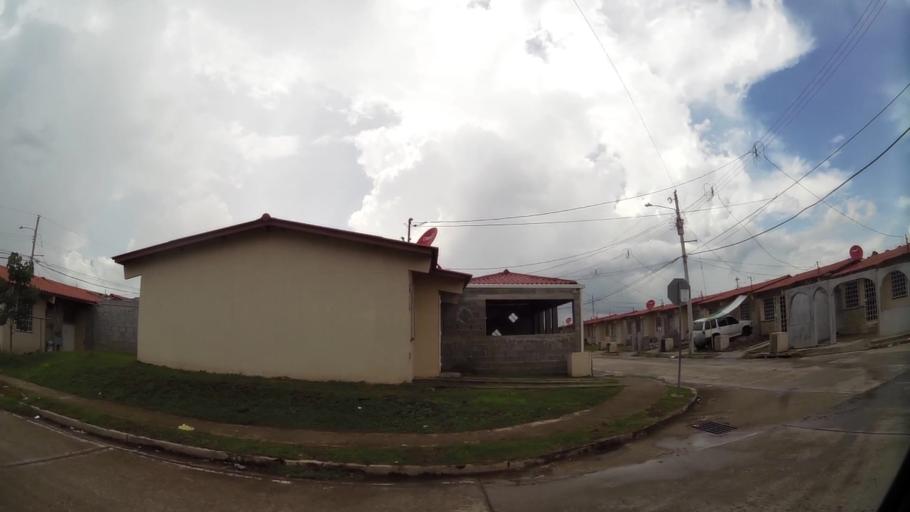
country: PA
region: Panama
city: Cabra Numero Uno
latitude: 9.1220
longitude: -79.3407
